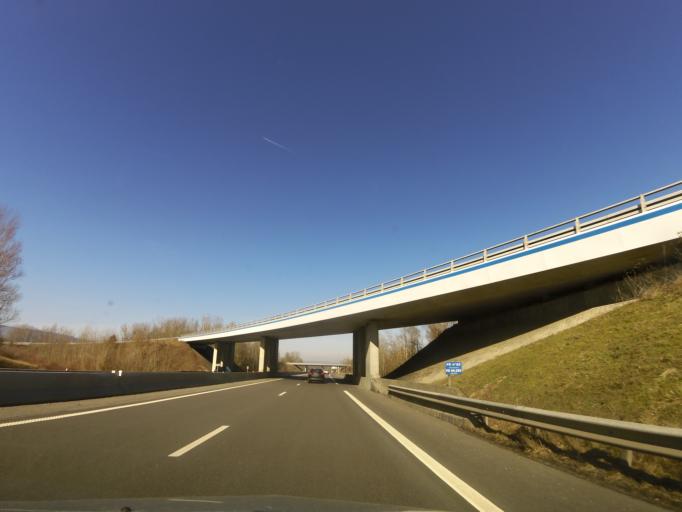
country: FR
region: Rhone-Alpes
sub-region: Departement de la Haute-Savoie
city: Contamine-sur-Arve
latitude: 46.1197
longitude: 6.3316
